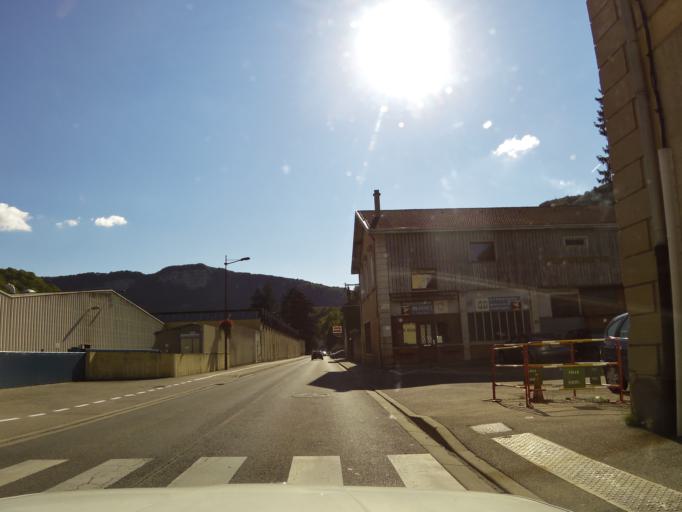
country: FR
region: Rhone-Alpes
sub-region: Departement de l'Ain
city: Saint-Rambert-en-Bugey
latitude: 45.9433
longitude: 5.4341
